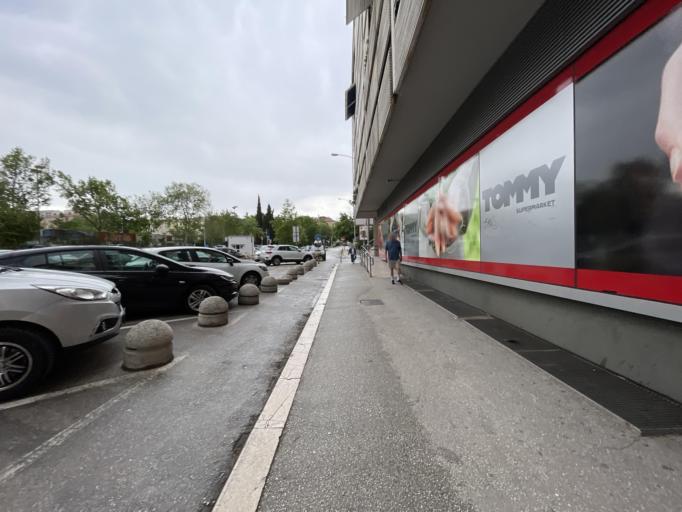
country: HR
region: Splitsko-Dalmatinska
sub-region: Grad Split
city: Split
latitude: 43.5122
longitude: 16.4361
